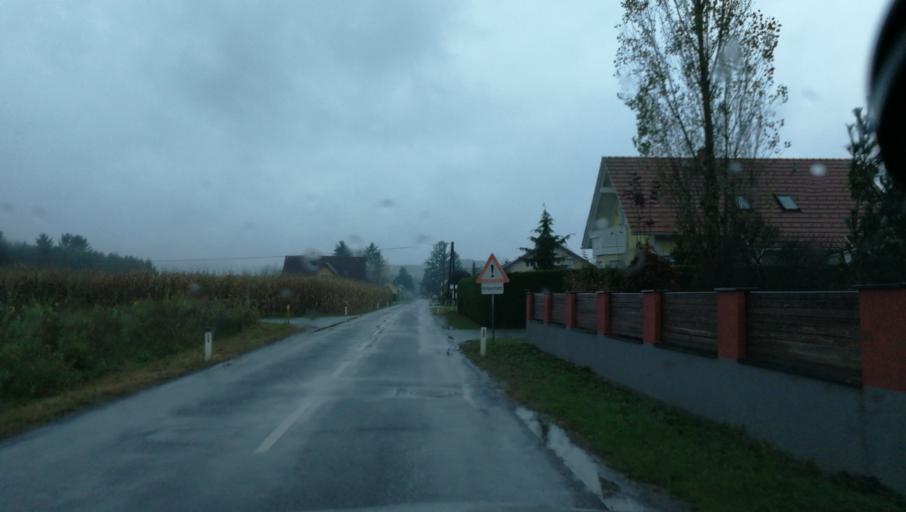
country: AT
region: Styria
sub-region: Politischer Bezirk Leibnitz
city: Sankt Veit am Vogau
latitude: 46.7368
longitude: 15.6123
